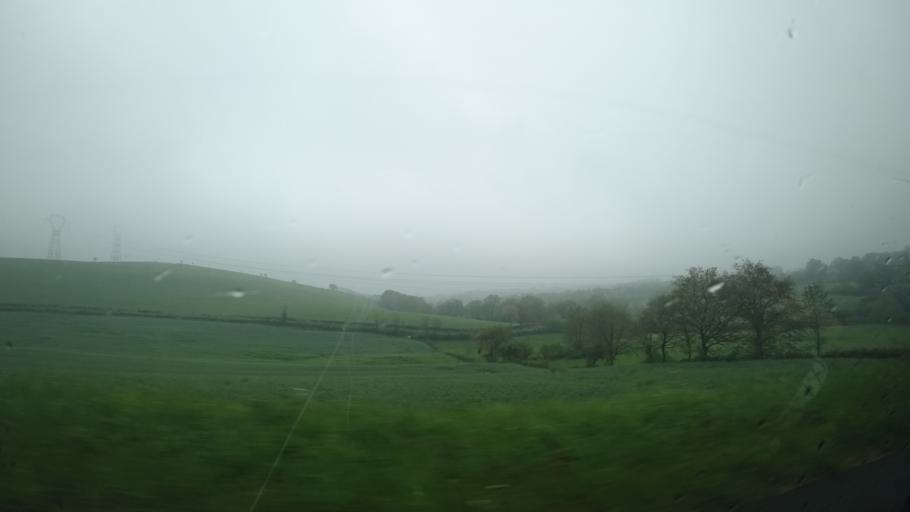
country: FR
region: Midi-Pyrenees
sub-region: Departement de l'Aveyron
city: Laissac
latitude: 44.3289
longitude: 2.7820
